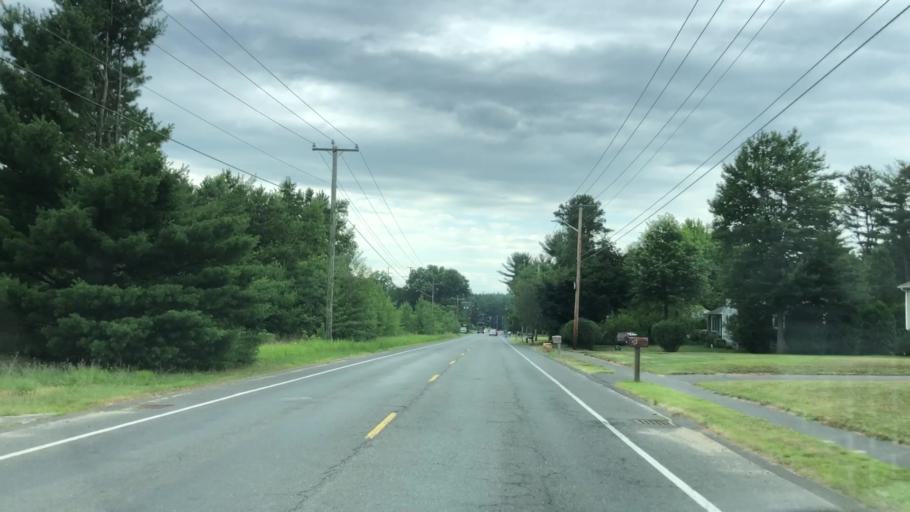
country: US
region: Massachusetts
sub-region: Hampshire County
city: Southampton
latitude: 42.2100
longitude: -72.6900
